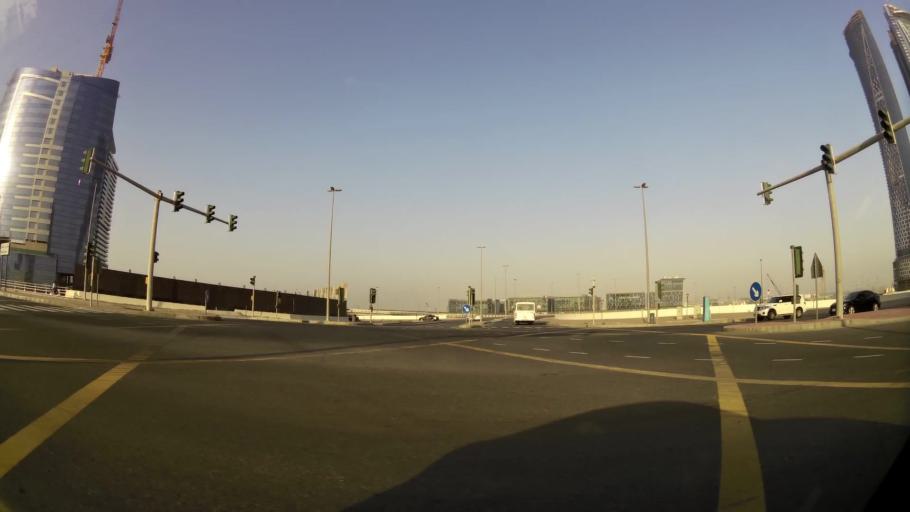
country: AE
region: Dubai
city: Dubai
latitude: 25.1896
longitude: 55.2897
